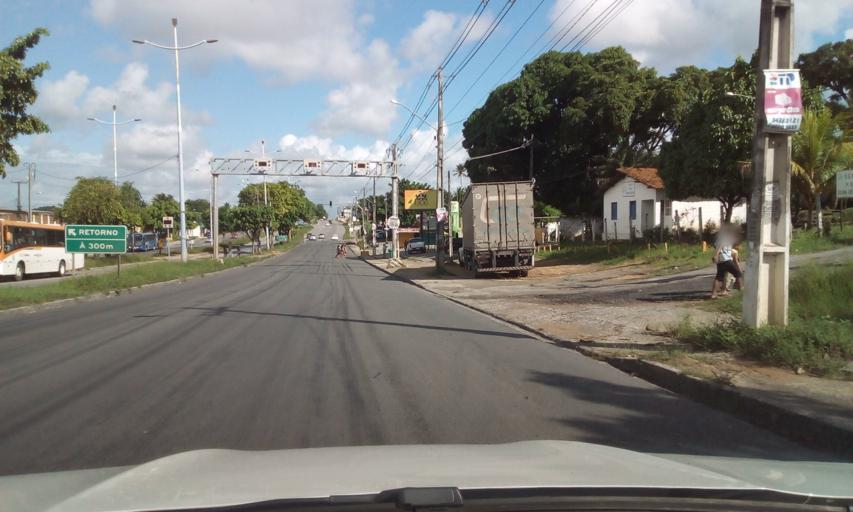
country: BR
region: Pernambuco
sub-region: Igarassu
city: Igarassu
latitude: -7.8549
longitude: -34.9089
